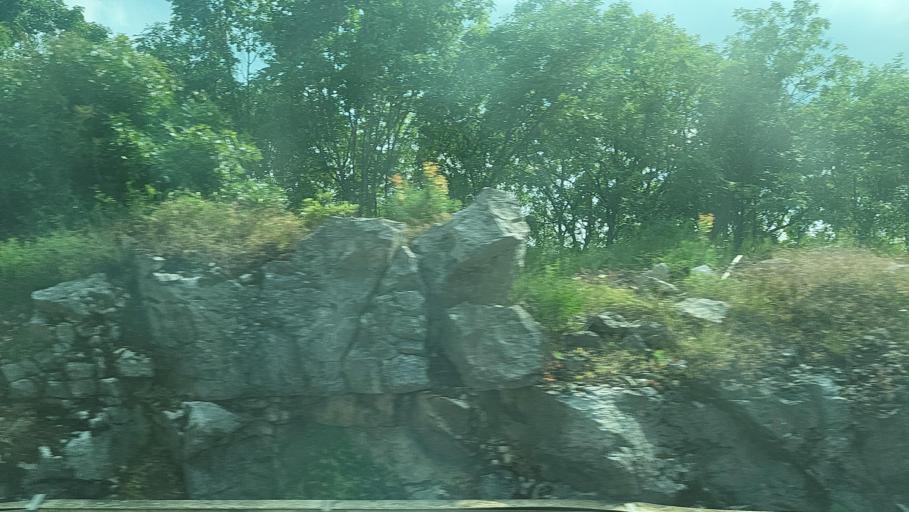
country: IT
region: Friuli Venezia Giulia
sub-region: Provincia di Trieste
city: Aurisina
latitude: 45.7429
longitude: 13.6706
